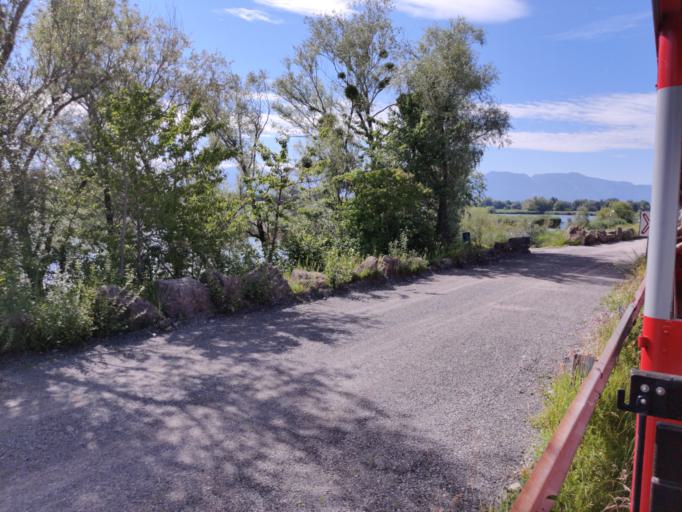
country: AT
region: Vorarlberg
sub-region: Politischer Bezirk Bregenz
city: Hard
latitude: 47.4985
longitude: 9.6721
